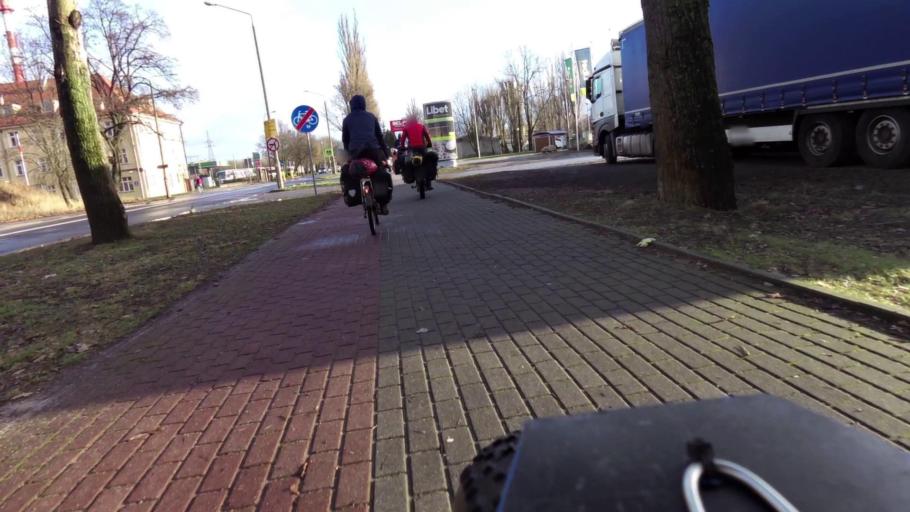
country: PL
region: Lubusz
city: Gorzow Wielkopolski
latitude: 52.7364
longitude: 15.2029
